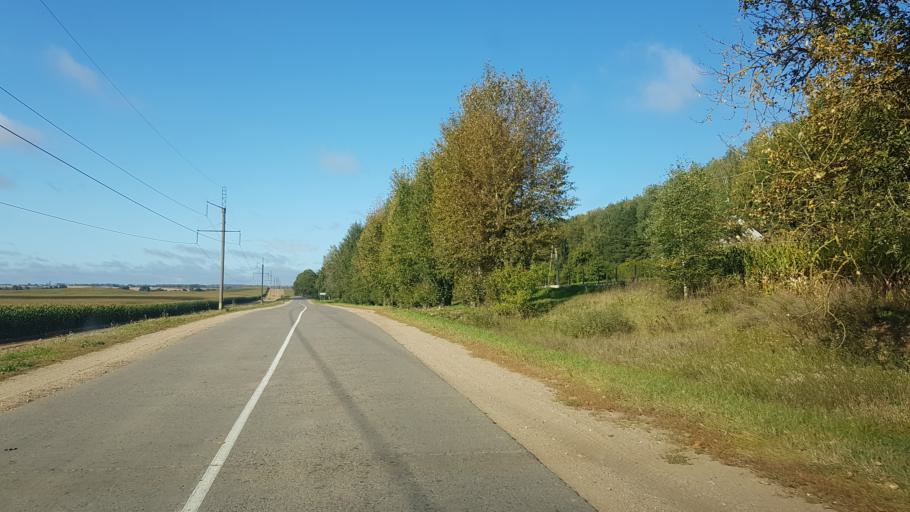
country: BY
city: Fanipol
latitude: 53.7365
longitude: 27.2351
